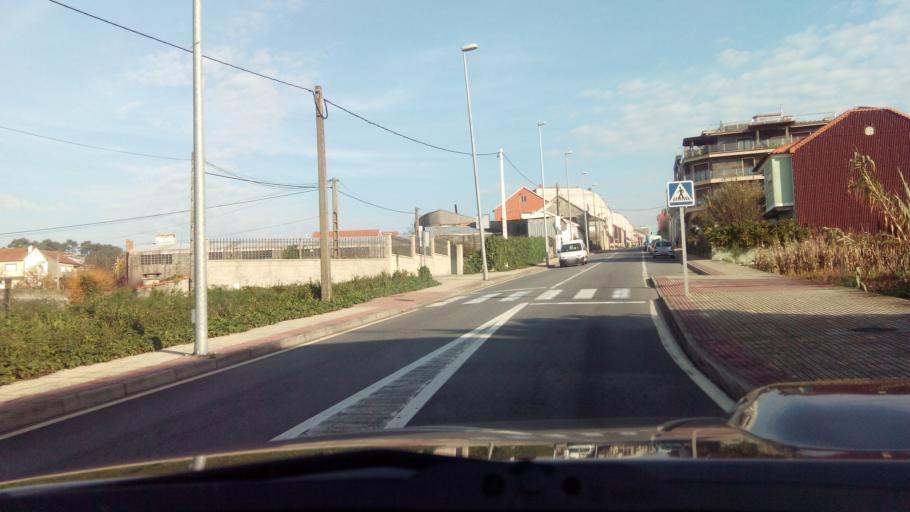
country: ES
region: Galicia
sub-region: Provincia de Pontevedra
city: Marin
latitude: 42.3639
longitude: -8.7365
